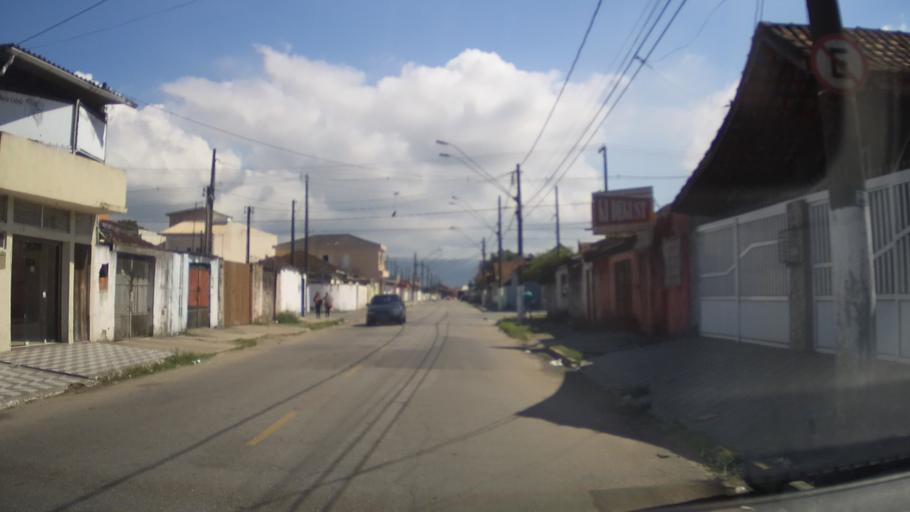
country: BR
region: Sao Paulo
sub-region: Praia Grande
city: Praia Grande
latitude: -24.0082
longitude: -46.4405
